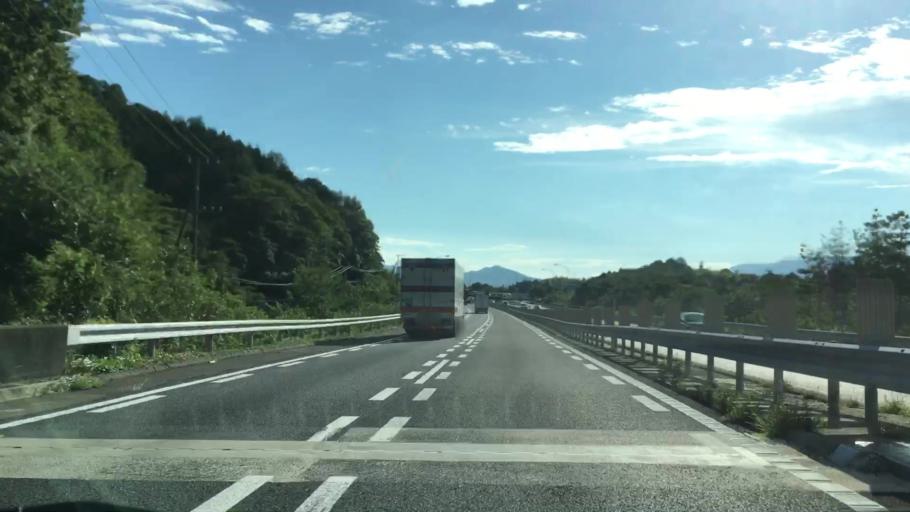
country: JP
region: Yamaguchi
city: Iwakuni
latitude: 34.1019
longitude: 132.1062
